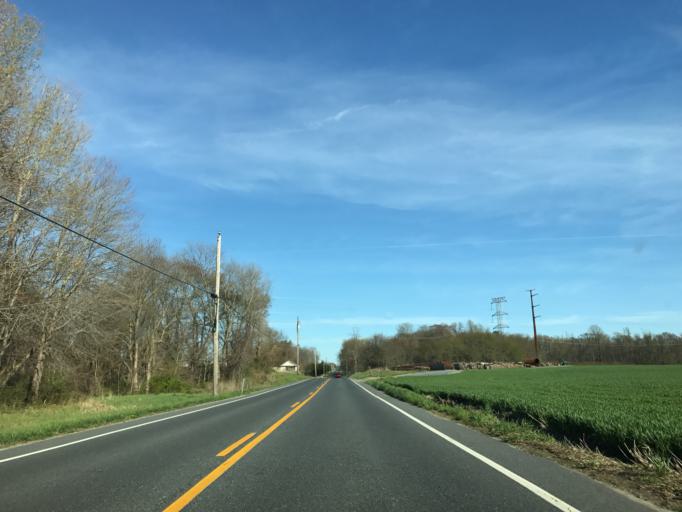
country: US
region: Maryland
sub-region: Caroline County
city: Greensboro
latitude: 39.0355
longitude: -75.7775
